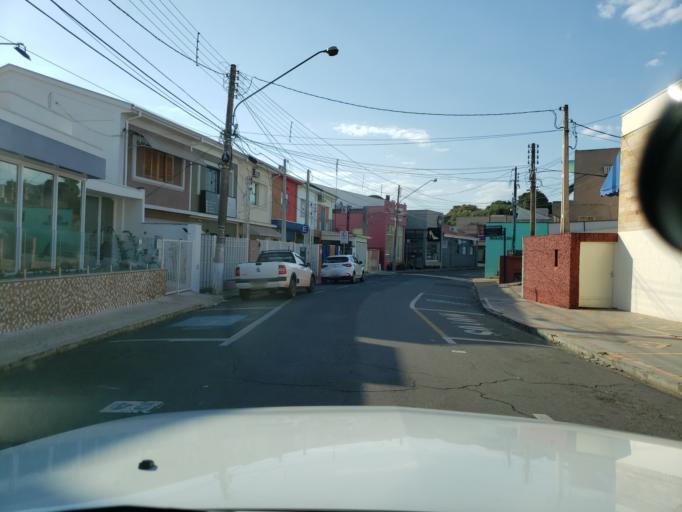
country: BR
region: Sao Paulo
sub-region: Moji-Guacu
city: Mogi-Gaucu
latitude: -22.3707
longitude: -46.9415
